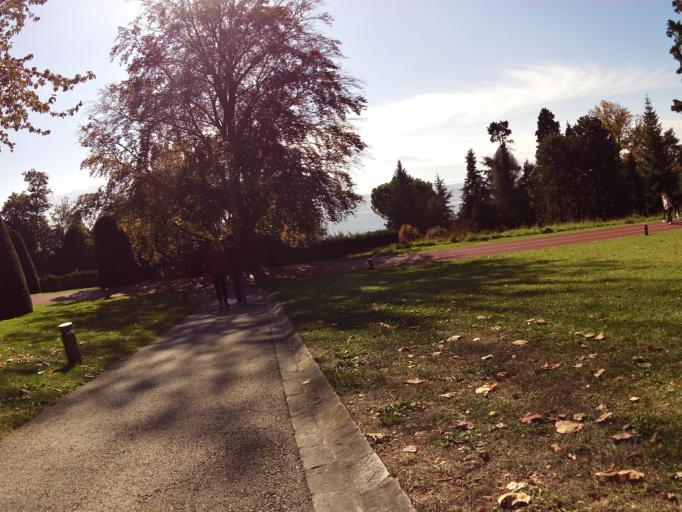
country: CH
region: Vaud
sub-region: Lausanne District
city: Lausanne
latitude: 46.5087
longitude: 6.6329
